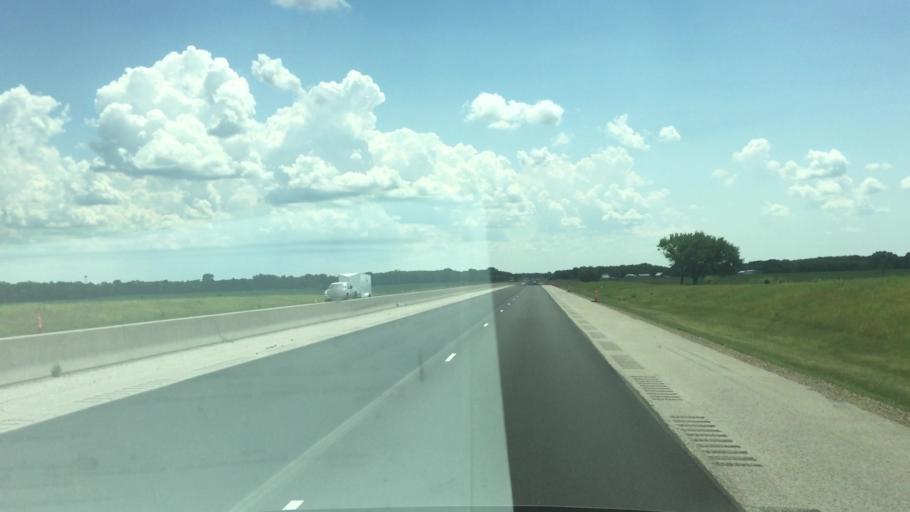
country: US
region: Kansas
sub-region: Lyon County
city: Emporia
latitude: 38.5321
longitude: -96.1363
